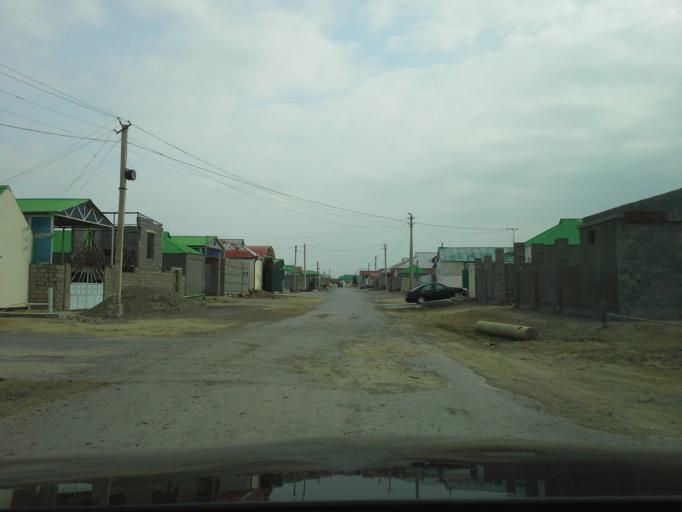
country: TM
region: Ahal
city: Abadan
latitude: 38.0397
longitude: 58.2506
